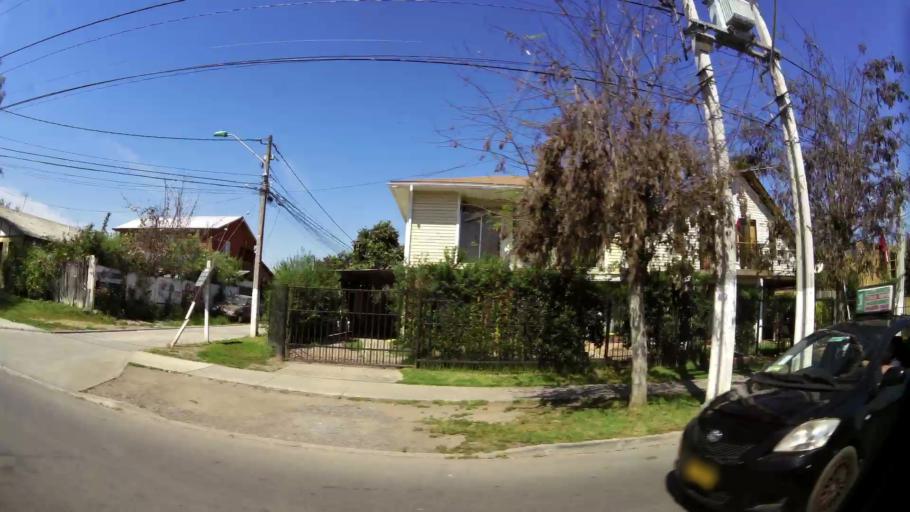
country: CL
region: Santiago Metropolitan
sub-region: Provincia de Talagante
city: Talagante
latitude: -33.6520
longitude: -70.9075
